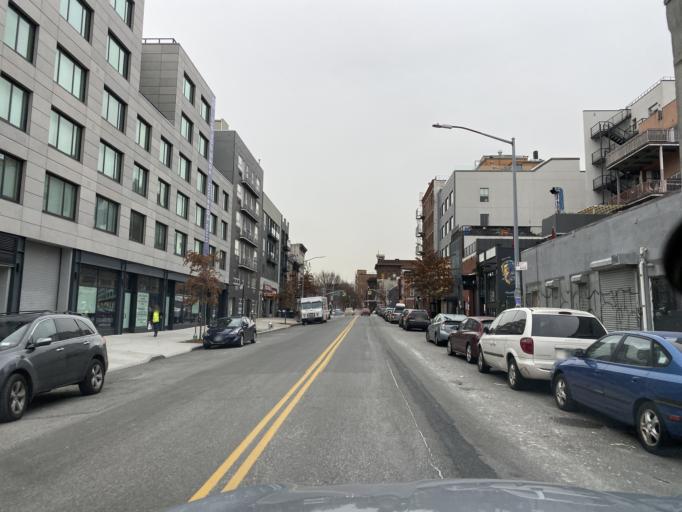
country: US
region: New York
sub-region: Queens County
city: Long Island City
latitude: 40.7166
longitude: -73.9631
